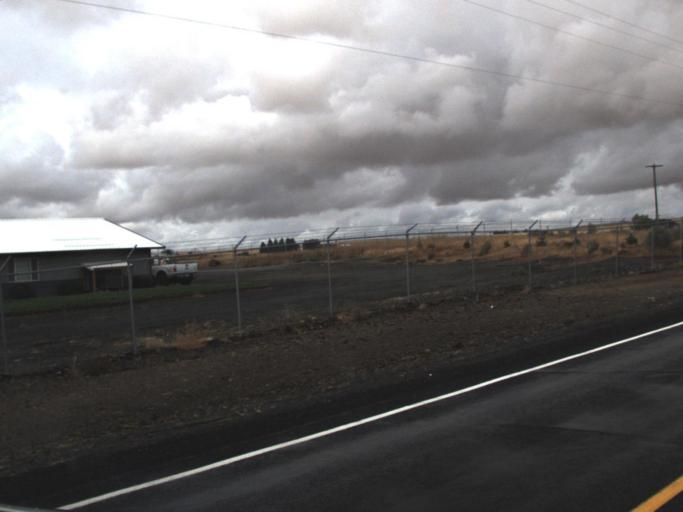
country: US
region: Washington
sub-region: Spokane County
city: Medical Lake
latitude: 47.6808
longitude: -117.8793
